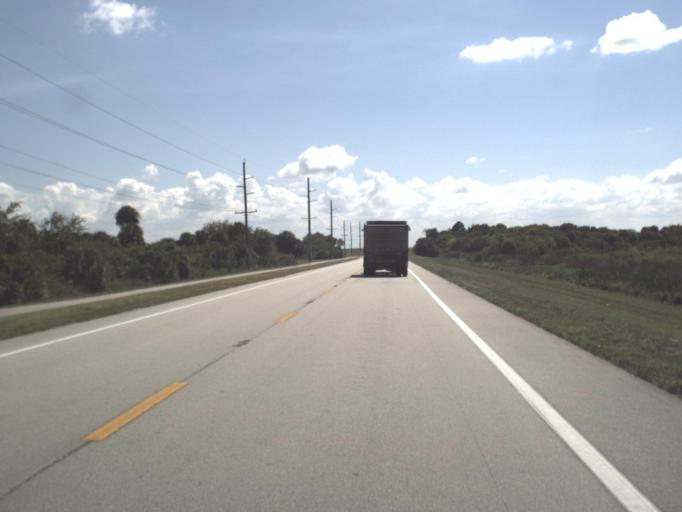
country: US
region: Florida
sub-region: Glades County
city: Moore Haven
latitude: 26.9313
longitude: -81.1223
